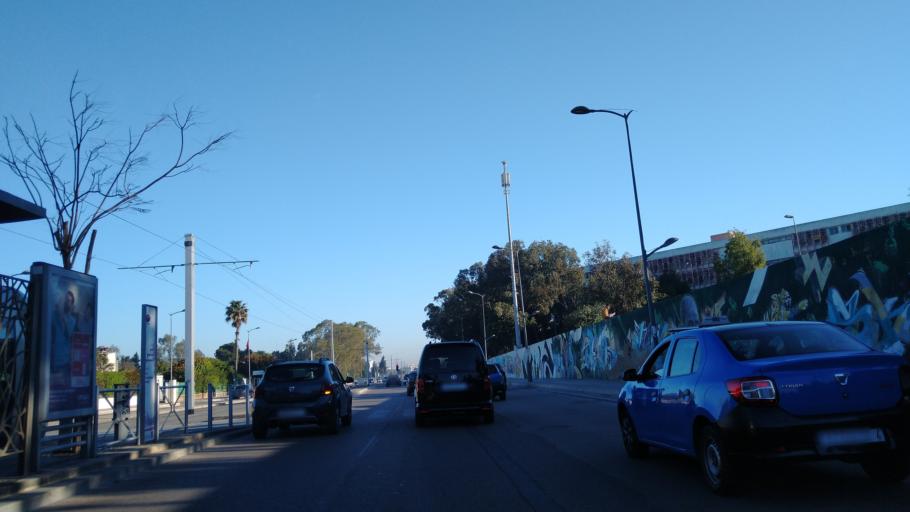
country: MA
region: Rabat-Sale-Zemmour-Zaer
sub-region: Rabat
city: Rabat
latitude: 33.9861
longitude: -6.8608
